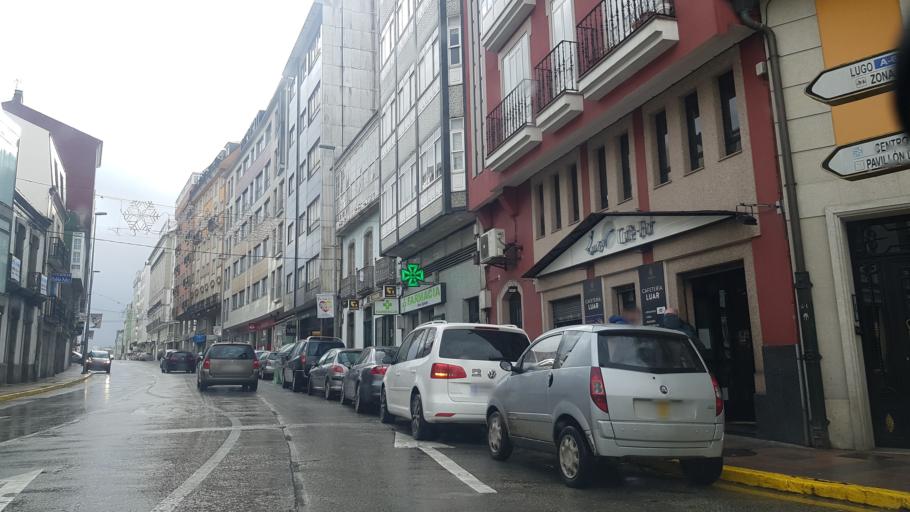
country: ES
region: Galicia
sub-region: Provincia de Lugo
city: Vilalba
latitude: 43.2976
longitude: -7.6820
